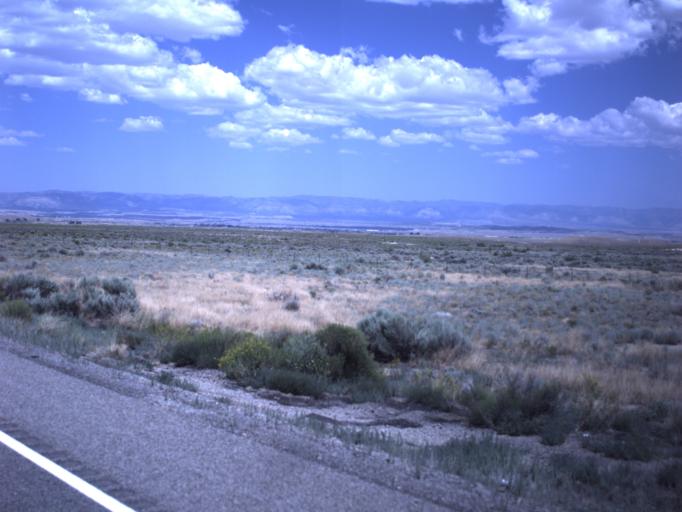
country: US
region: Utah
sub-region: Carbon County
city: Price
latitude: 39.4874
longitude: -110.8492
